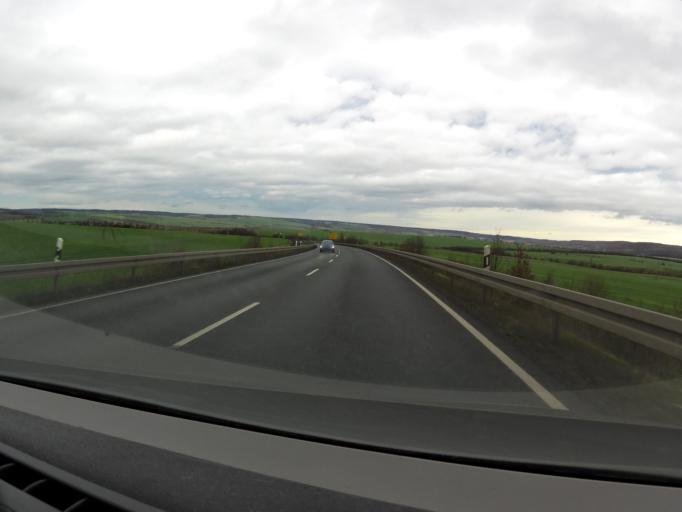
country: DE
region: Saxony-Anhalt
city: Sangerhausen
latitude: 51.4653
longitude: 11.3262
